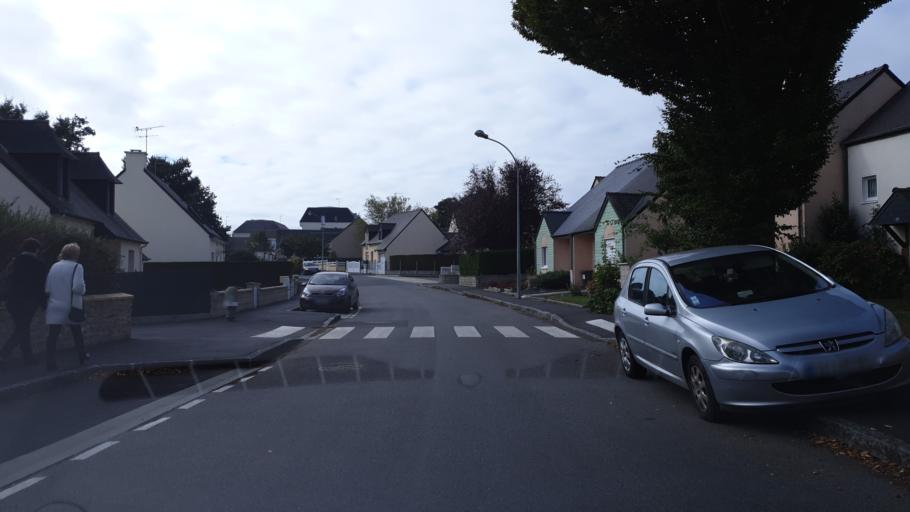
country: FR
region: Brittany
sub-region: Departement d'Ille-et-Vilaine
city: Janze
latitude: 47.9616
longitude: -1.4922
